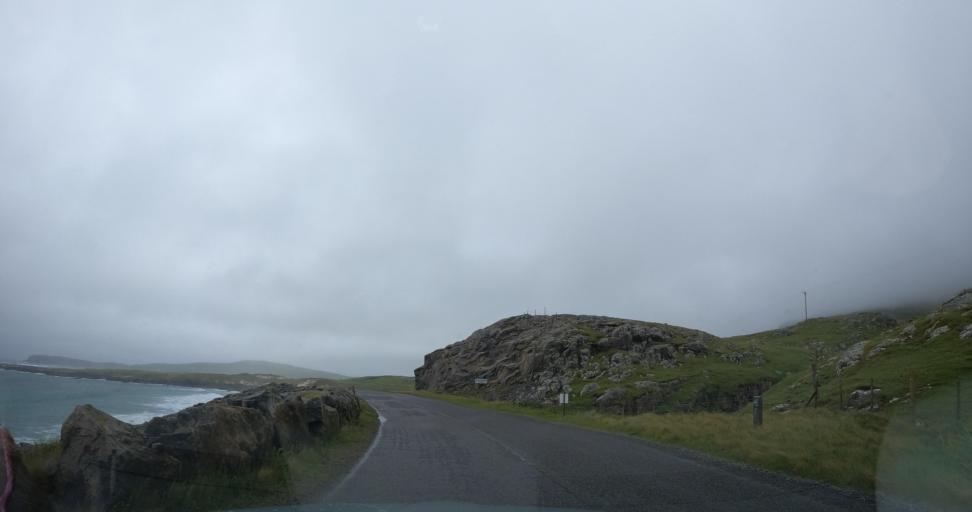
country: GB
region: Scotland
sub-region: Eilean Siar
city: Barra
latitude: 56.9911
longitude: -7.5089
